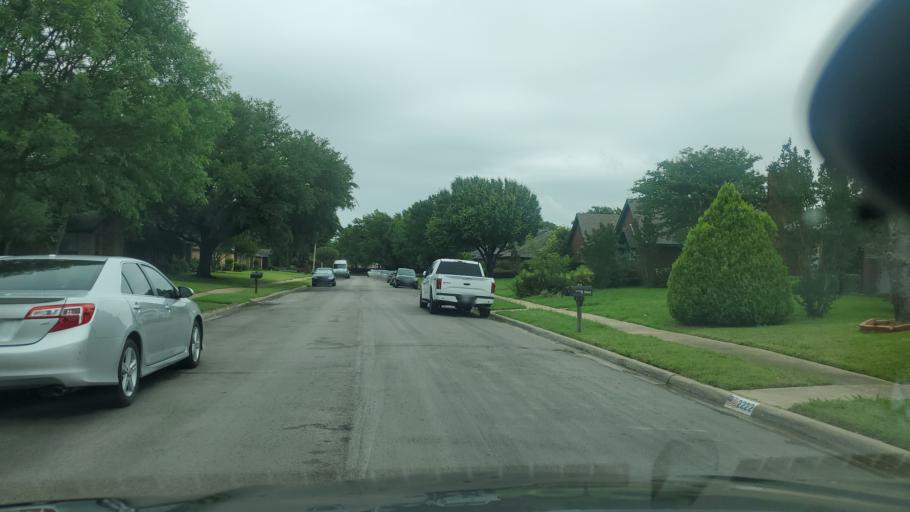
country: US
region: Texas
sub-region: Dallas County
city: Garland
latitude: 32.9391
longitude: -96.6327
